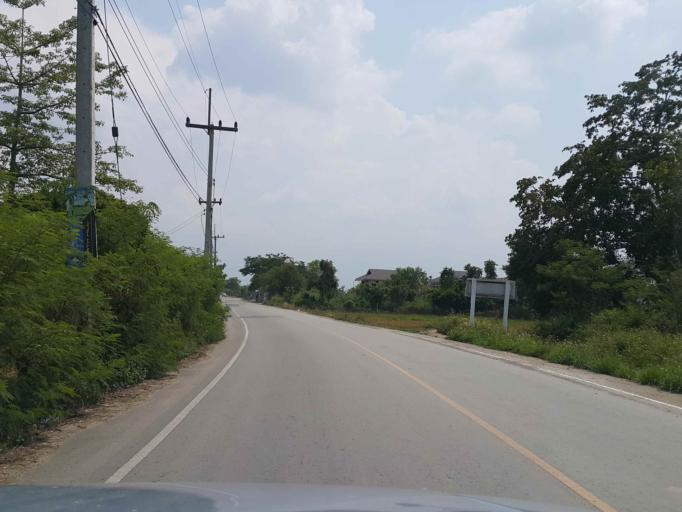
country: TH
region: Chiang Mai
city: Hang Dong
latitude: 18.6998
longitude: 98.9646
